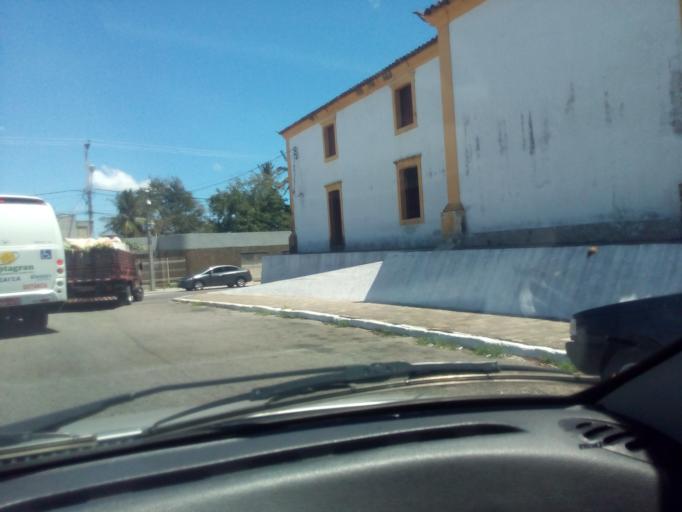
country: BR
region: Rio Grande do Norte
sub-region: Sao Goncalo Do Amarante
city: Sao Goncalo do Amarante
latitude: -5.7935
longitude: -35.3287
